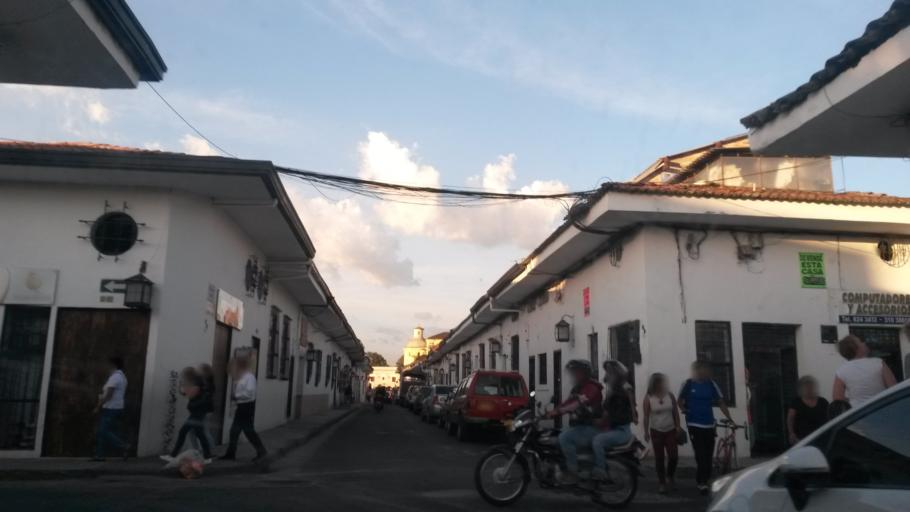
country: CO
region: Cauca
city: Popayan
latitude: 2.4415
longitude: -76.6098
